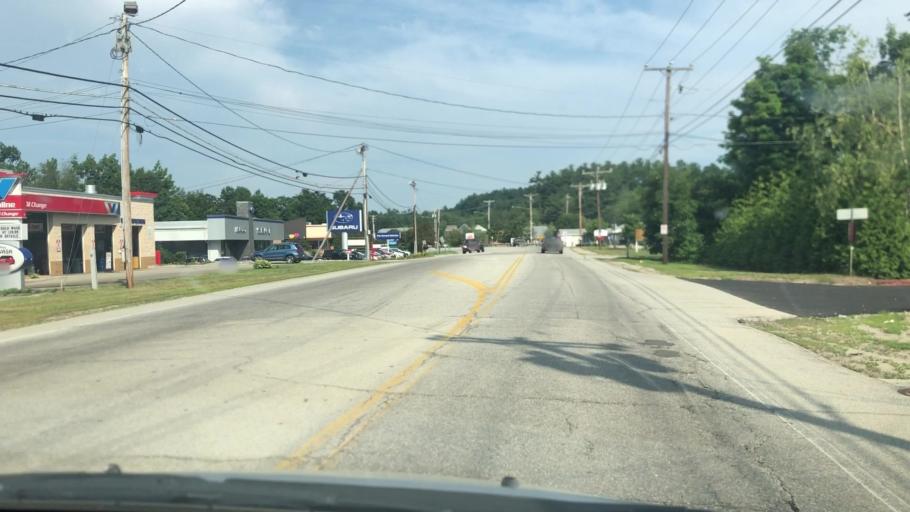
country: US
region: New Hampshire
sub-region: Hillsborough County
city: Milford
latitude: 42.8241
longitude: -71.6282
